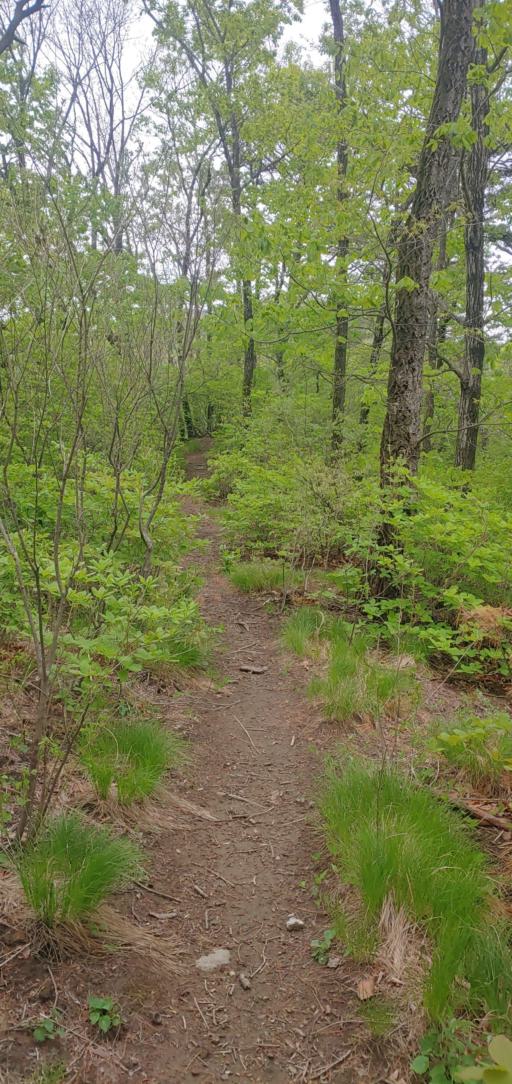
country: KR
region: Gyeongsangbuk-do
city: Eisen
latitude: 36.8455
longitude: 128.4649
